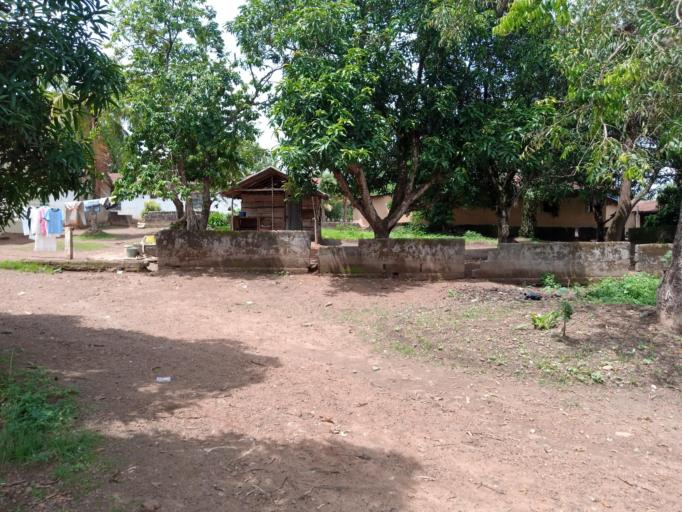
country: SL
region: Southern Province
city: Bo
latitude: 7.9472
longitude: -11.7207
